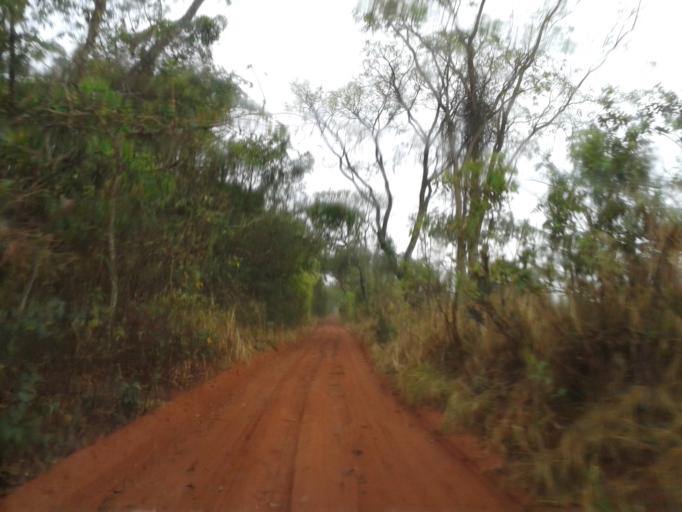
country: BR
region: Minas Gerais
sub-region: Campina Verde
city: Campina Verde
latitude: -19.3502
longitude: -49.5319
